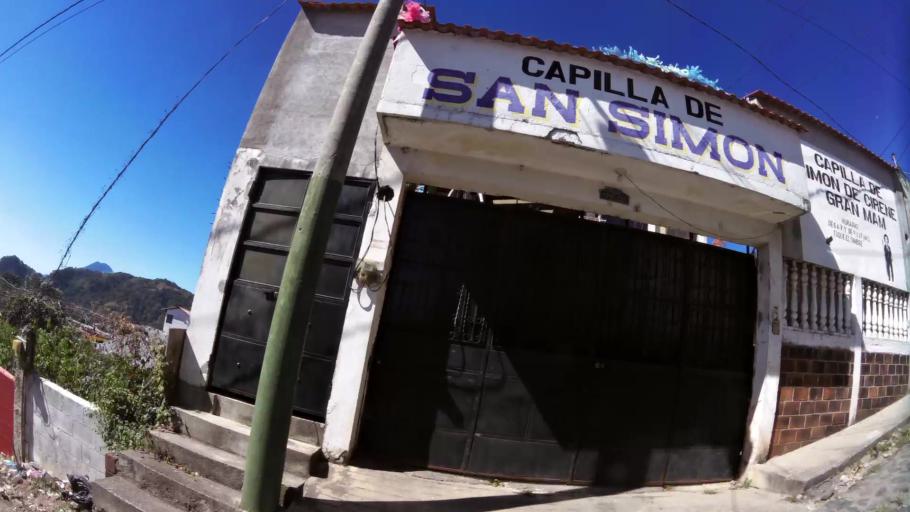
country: GT
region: Solola
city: Solola
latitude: 14.7670
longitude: -91.1821
